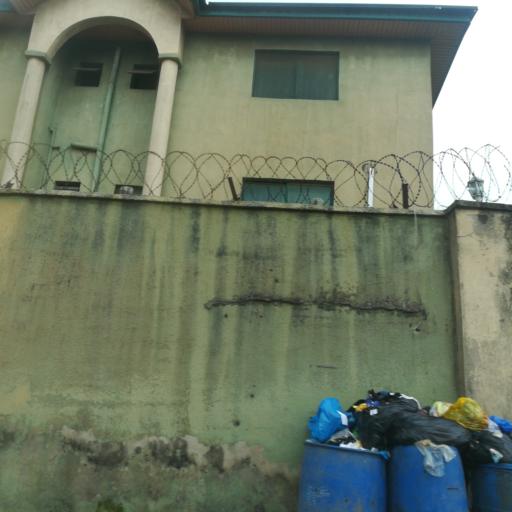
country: NG
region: Lagos
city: Agege
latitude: 6.5939
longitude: 3.2966
